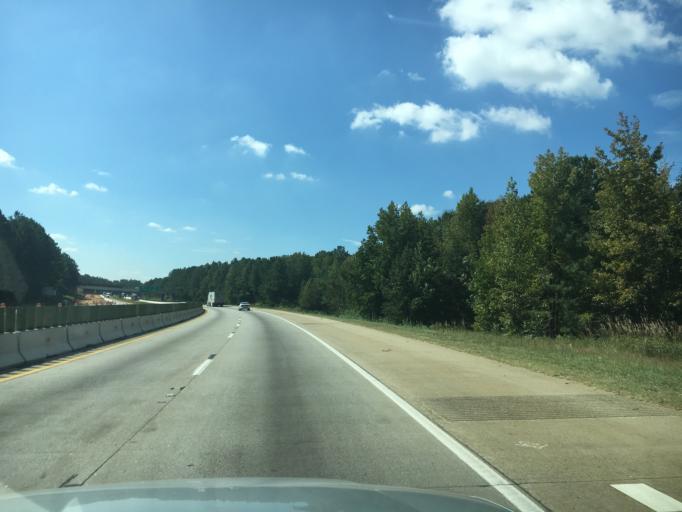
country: US
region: South Carolina
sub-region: Spartanburg County
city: Southern Shops
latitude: 34.9898
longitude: -82.0005
